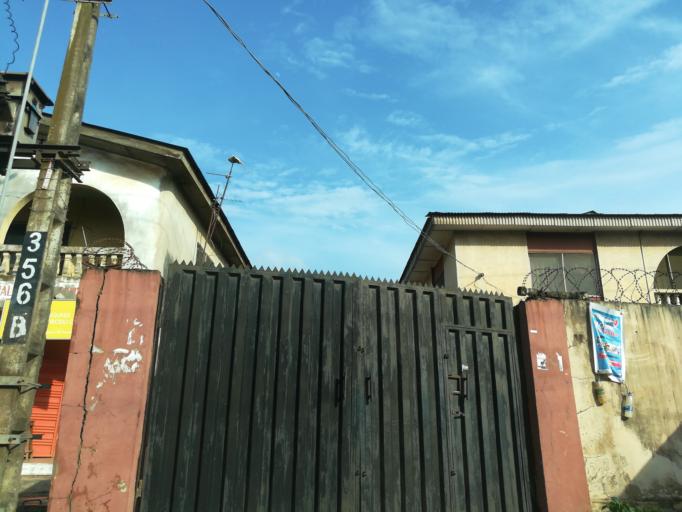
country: NG
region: Lagos
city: Ojota
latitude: 6.6058
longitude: 3.4208
